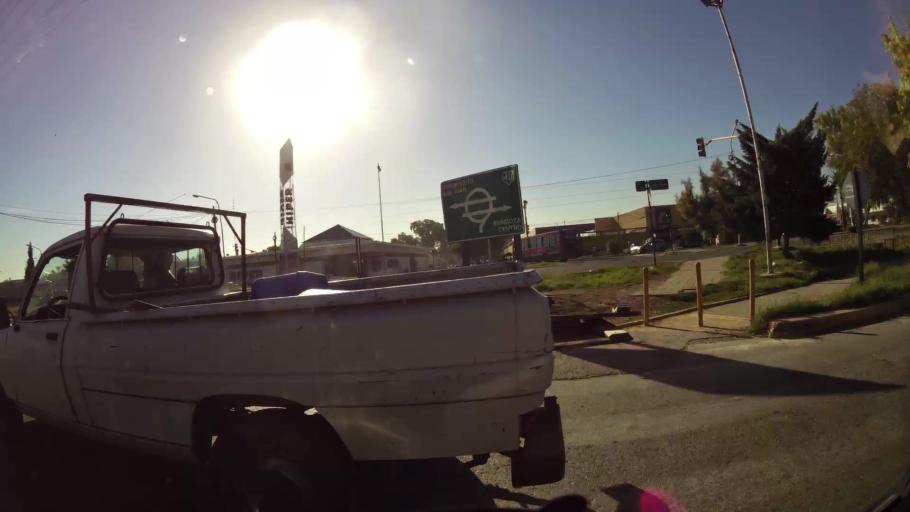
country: AR
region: Mendoza
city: Las Heras
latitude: -32.8556
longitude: -68.8071
